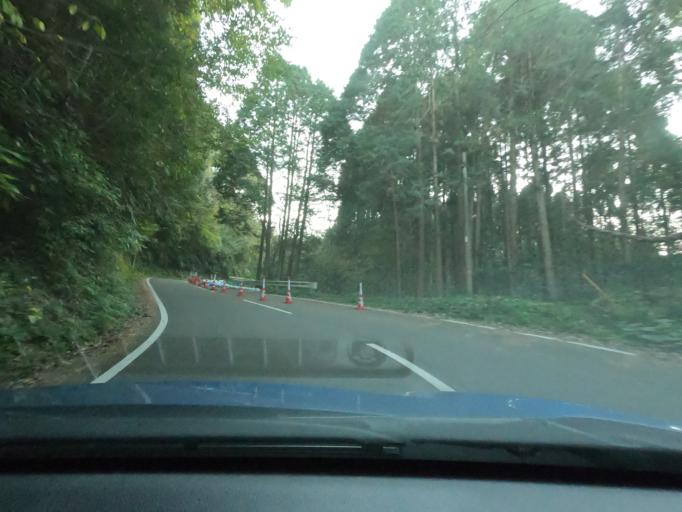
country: JP
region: Kagoshima
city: Satsumasendai
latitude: 31.8211
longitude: 130.4794
